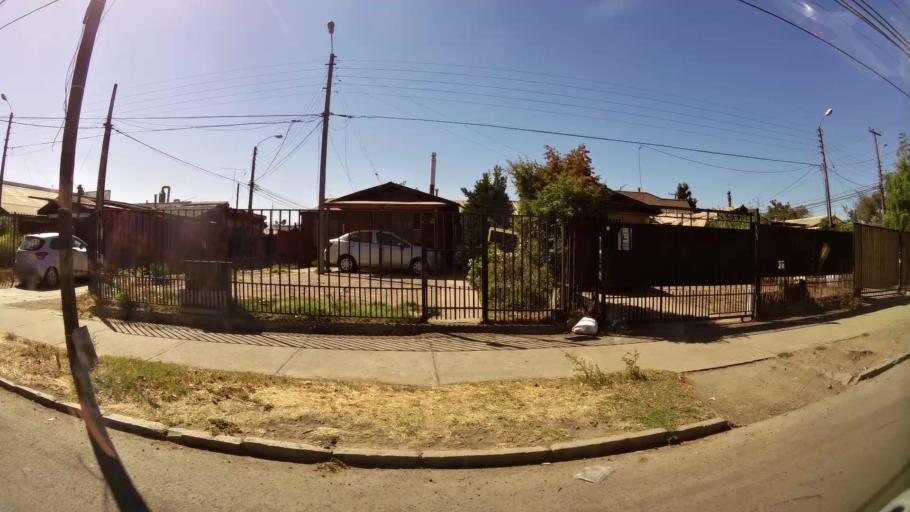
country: CL
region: O'Higgins
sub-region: Provincia de Cachapoal
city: Rancagua
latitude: -34.1803
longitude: -70.7454
